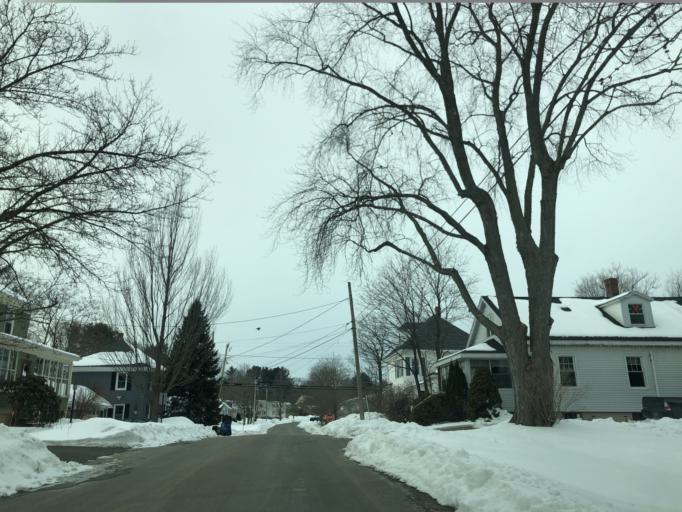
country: US
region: Maine
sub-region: Cumberland County
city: Westbrook
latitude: 43.6841
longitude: -70.3640
